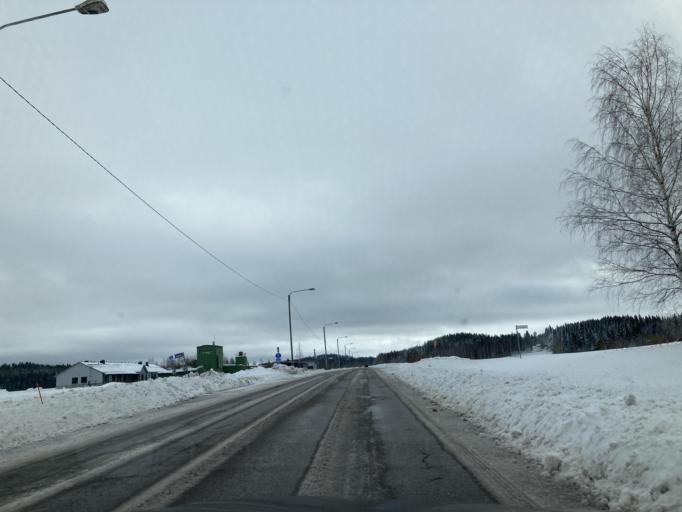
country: FI
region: Central Finland
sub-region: Jaemsae
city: Jaemsae
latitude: 61.8543
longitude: 25.2047
